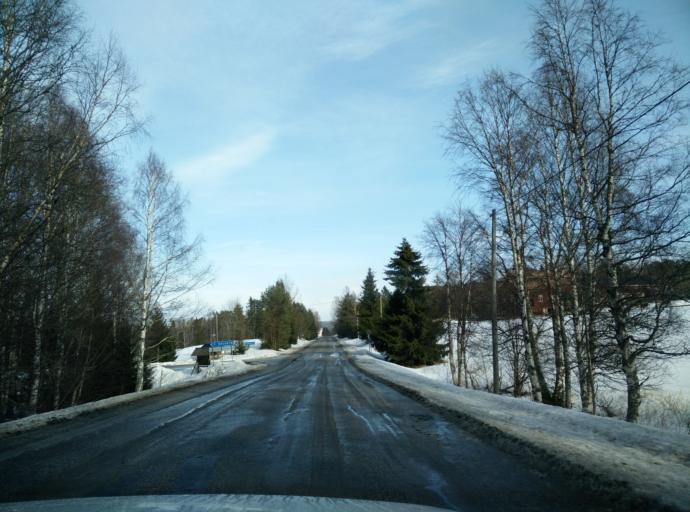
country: SE
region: Vaesternorrland
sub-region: Sundsvalls Kommun
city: Njurundabommen
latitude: 62.2144
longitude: 17.2960
